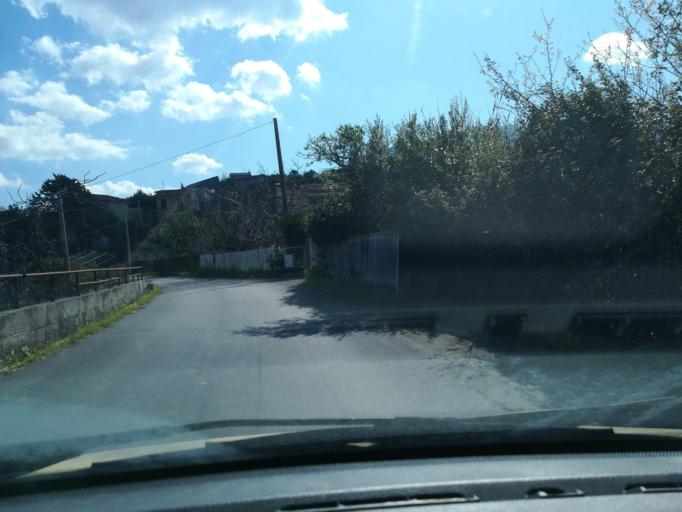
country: IT
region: Sicily
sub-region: Palermo
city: Cannizzaro-Favara
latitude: 38.0459
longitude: 13.2619
